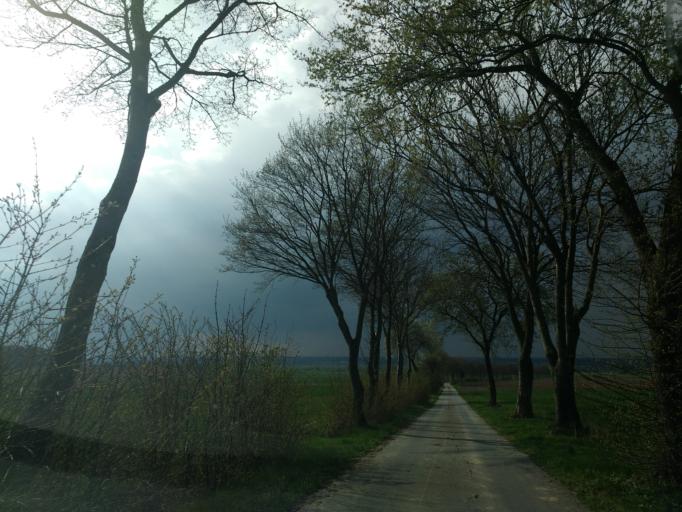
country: DE
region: North Rhine-Westphalia
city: Bad Lippspringe
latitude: 51.7593
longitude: 8.8581
